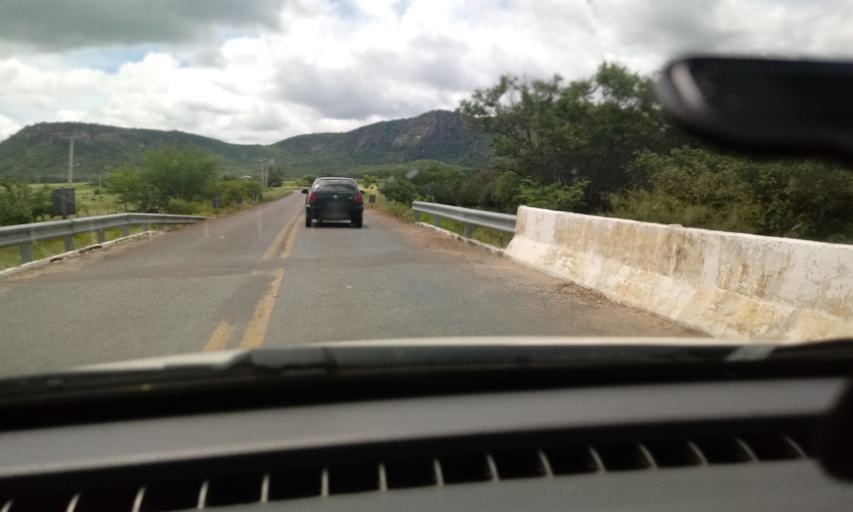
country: BR
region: Bahia
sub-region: Guanambi
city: Guanambi
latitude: -14.1509
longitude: -42.8264
